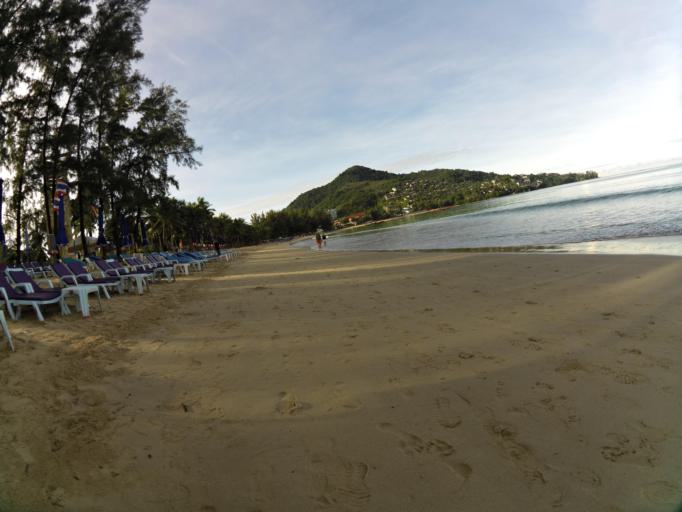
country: TH
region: Phuket
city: Patong
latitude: 7.9538
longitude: 98.2820
